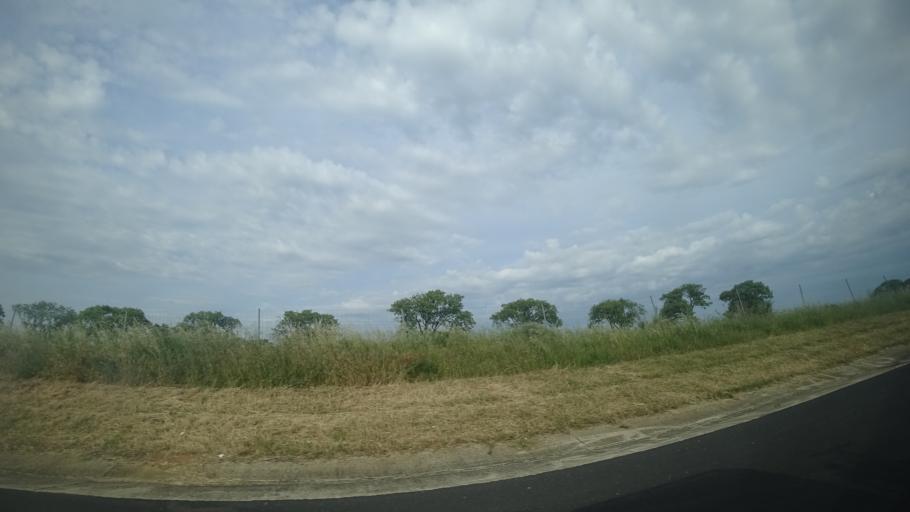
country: FR
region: Languedoc-Roussillon
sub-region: Departement de l'Herault
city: Aspiran
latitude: 43.5653
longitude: 3.4664
